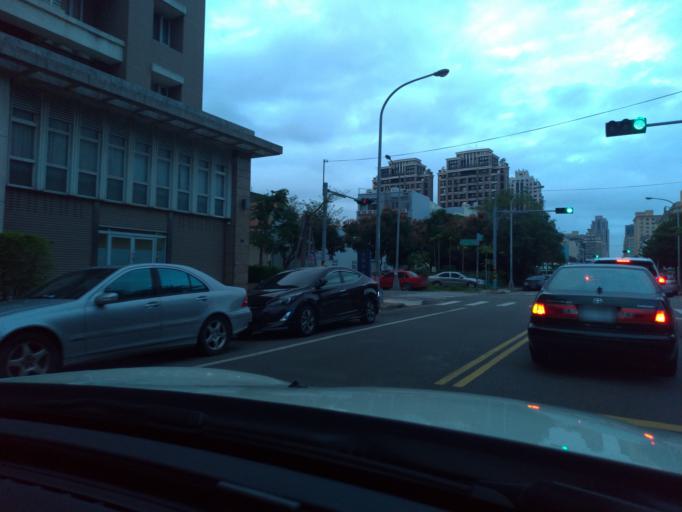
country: TW
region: Taiwan
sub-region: Hsinchu
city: Zhubei
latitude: 24.8165
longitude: 121.0224
